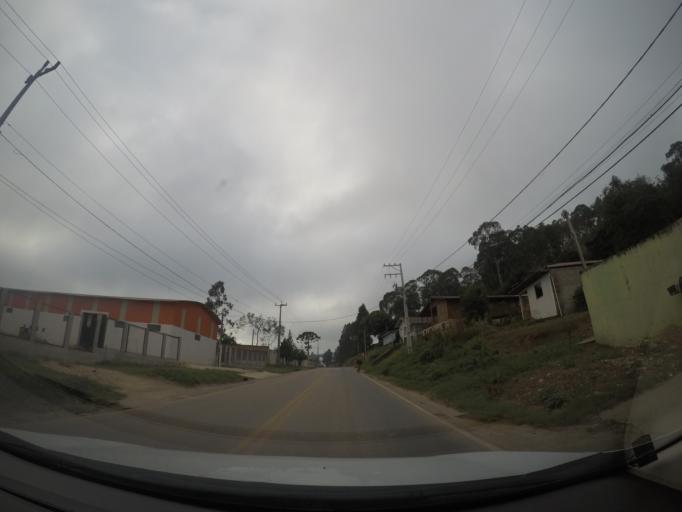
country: BR
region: Parana
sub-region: Colombo
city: Colombo
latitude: -25.2951
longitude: -49.2418
